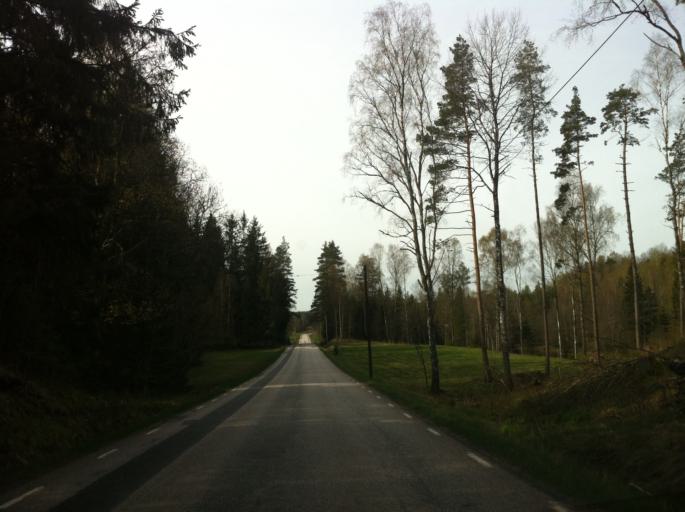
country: SE
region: Vaestra Goetaland
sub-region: Bollebygds Kommun
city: Bollebygd
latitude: 57.7473
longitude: 12.6085
